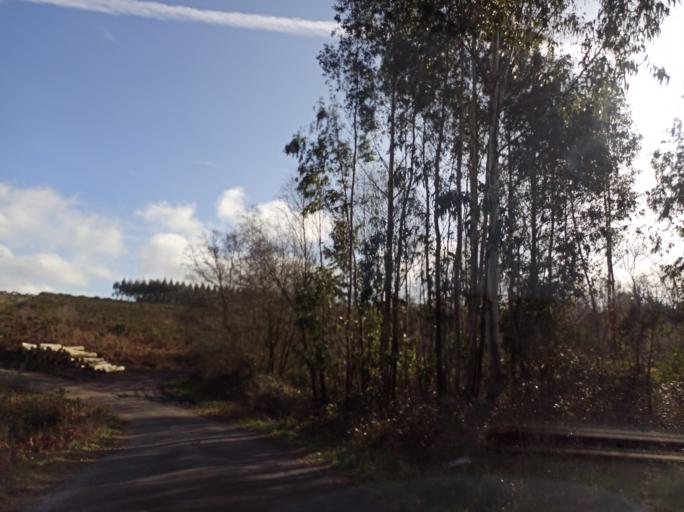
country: ES
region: Galicia
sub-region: Provincia da Coruna
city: Sobrado
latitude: 43.0792
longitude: -7.9526
